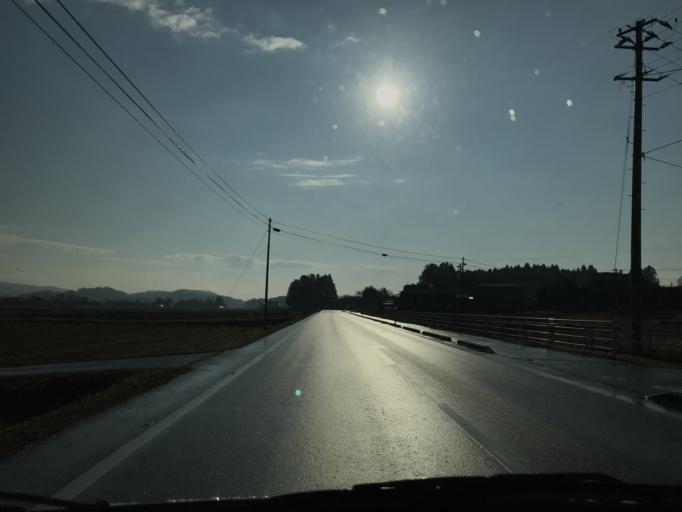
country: JP
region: Iwate
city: Ichinoseki
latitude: 38.7737
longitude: 141.1762
